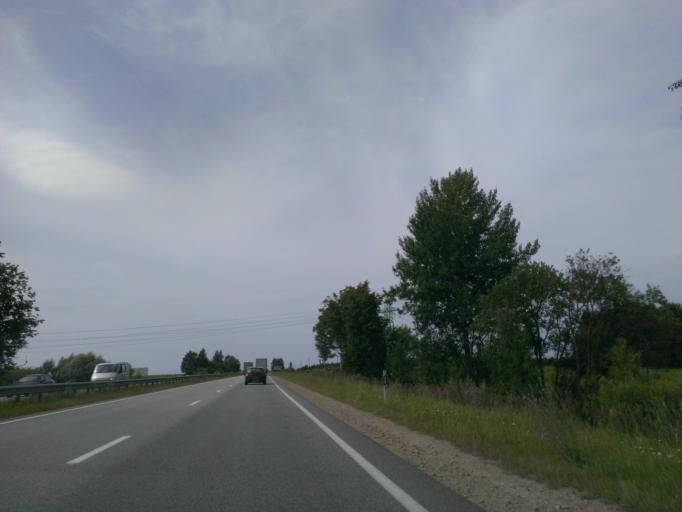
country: LV
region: Salaspils
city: Salaspils
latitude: 56.8462
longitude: 24.3799
